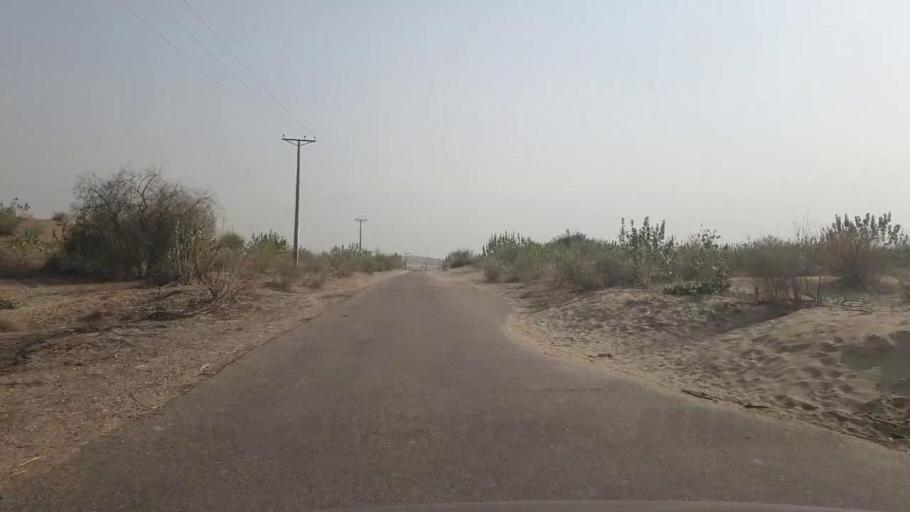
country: PK
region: Sindh
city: Chor
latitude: 25.5434
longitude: 69.9598
